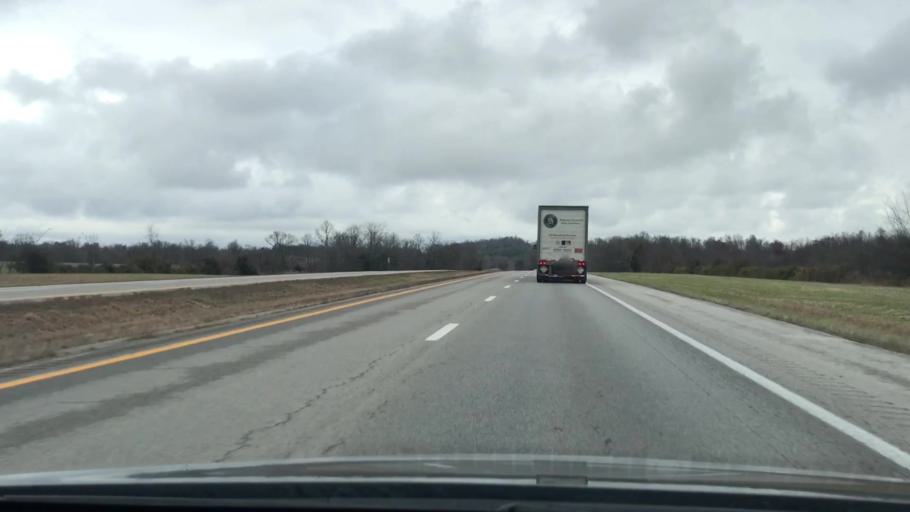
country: US
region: Kentucky
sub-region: Christian County
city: Hopkinsville
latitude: 36.9259
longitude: -87.4716
